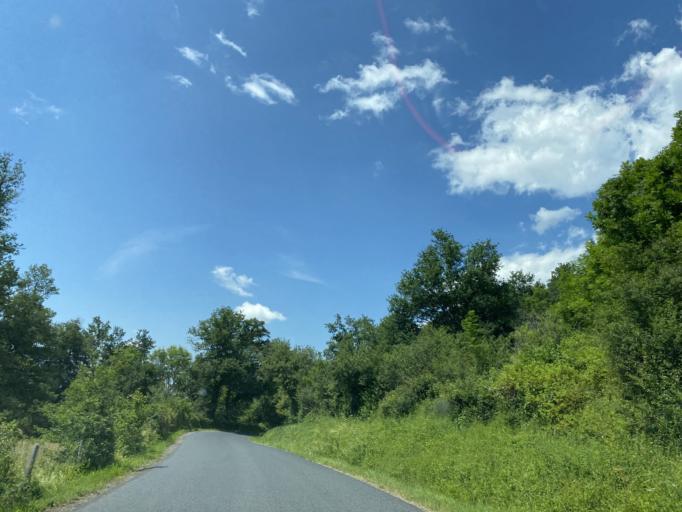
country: FR
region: Auvergne
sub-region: Departement du Puy-de-Dome
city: Courpiere
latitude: 45.7776
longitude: 3.5501
